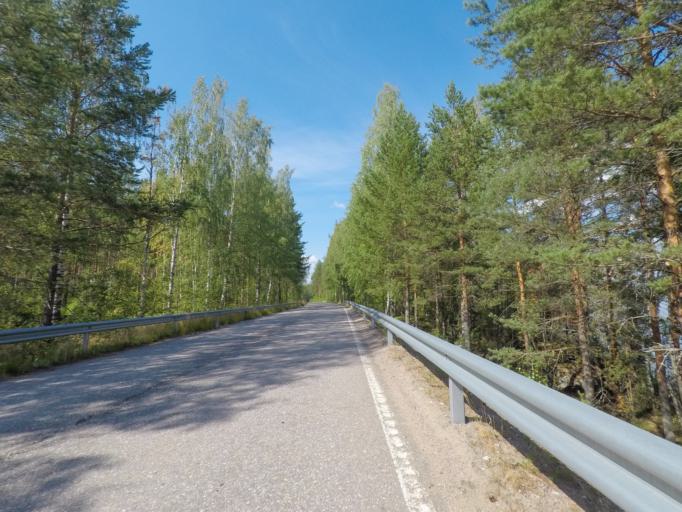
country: FI
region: Southern Savonia
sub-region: Mikkeli
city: Puumala
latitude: 61.4691
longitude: 28.1687
